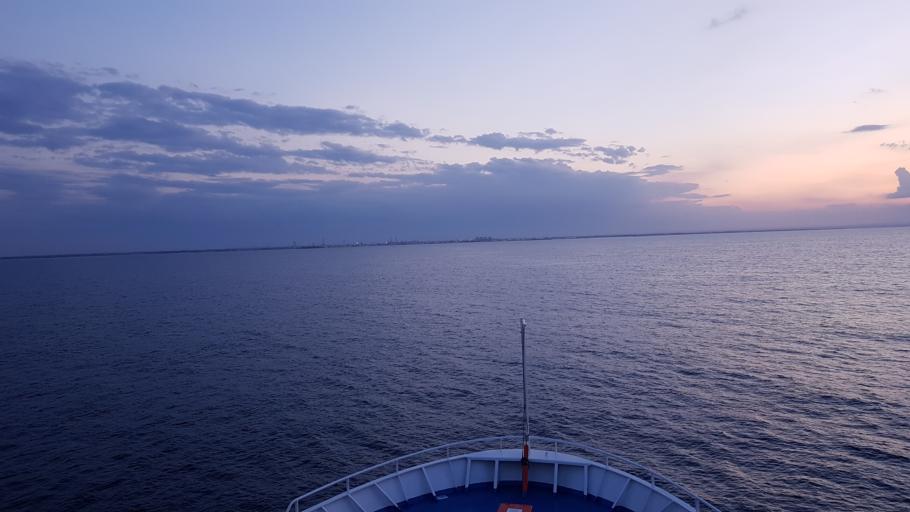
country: IT
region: Apulia
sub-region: Provincia di Brindisi
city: Materdomini
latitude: 40.6722
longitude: 18.0829
